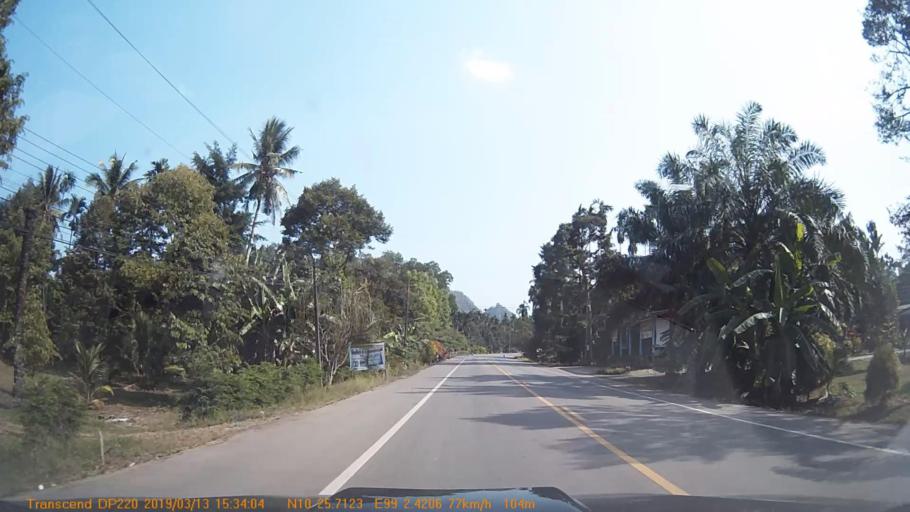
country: TH
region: Chumphon
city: Chumphon
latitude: 10.4280
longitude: 99.0405
